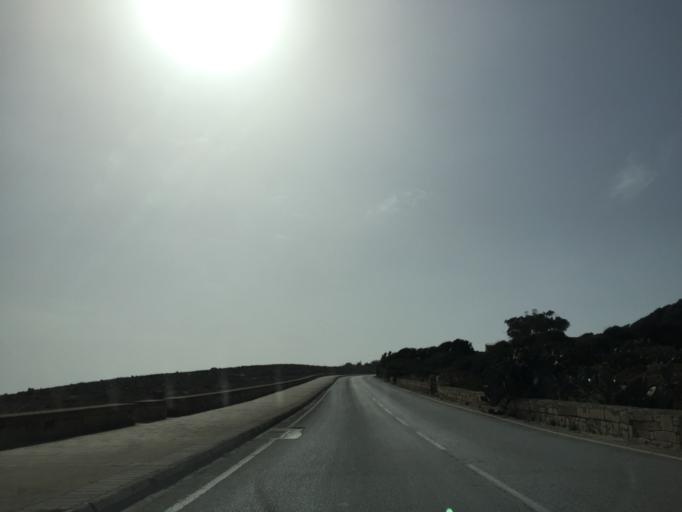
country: MT
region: Il-Qrendi
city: Qrendi
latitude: 35.8238
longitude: 14.4527
